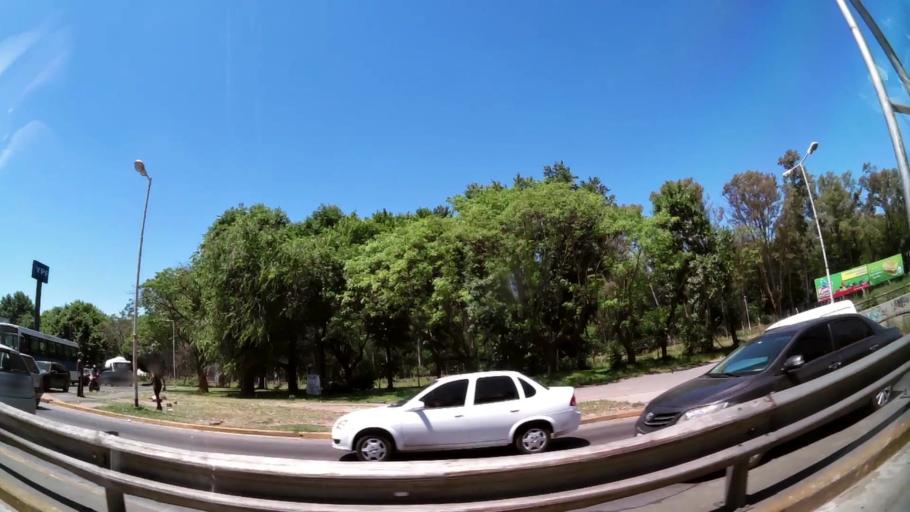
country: AR
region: Buenos Aires
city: Hurlingham
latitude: -34.5020
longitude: -58.6462
